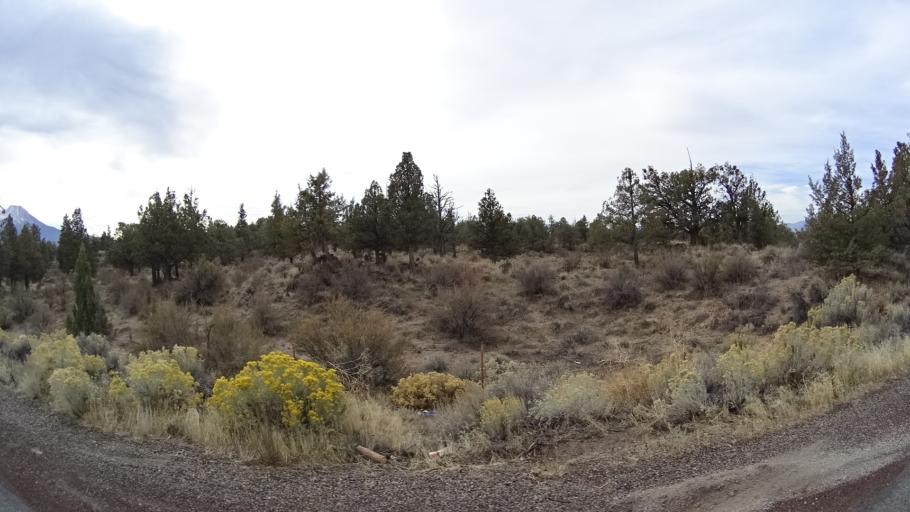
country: US
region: California
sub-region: Siskiyou County
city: Weed
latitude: 41.5893
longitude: -122.3027
